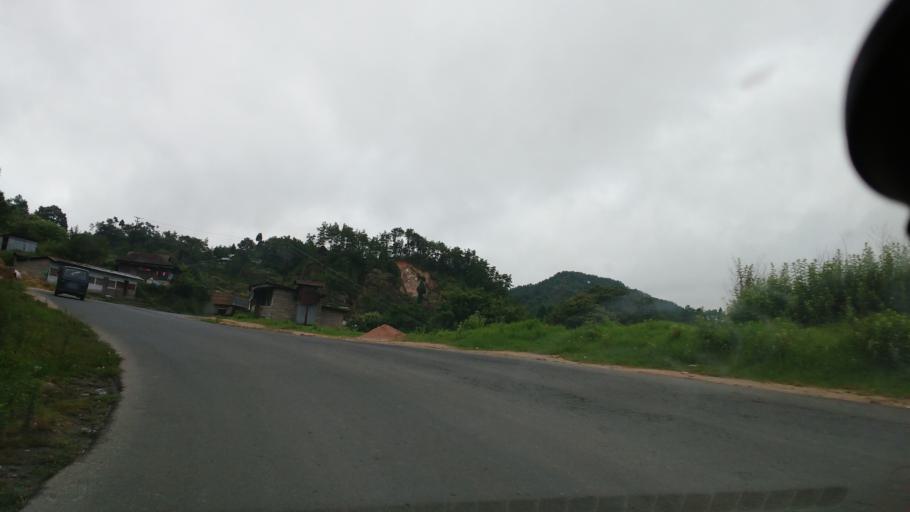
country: IN
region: Meghalaya
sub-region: East Khasi Hills
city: Shillong
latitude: 25.4914
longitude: 91.8211
